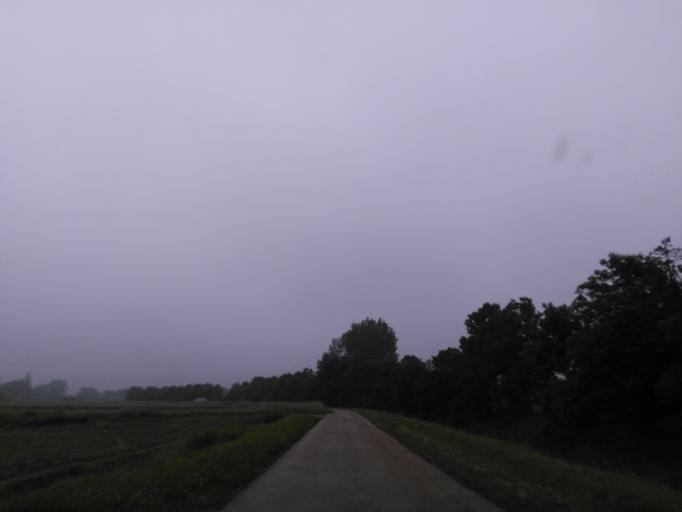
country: BE
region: Flanders
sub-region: Provincie Oost-Vlaanderen
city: Sint-Gillis-Waas
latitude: 51.2298
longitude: 4.1769
